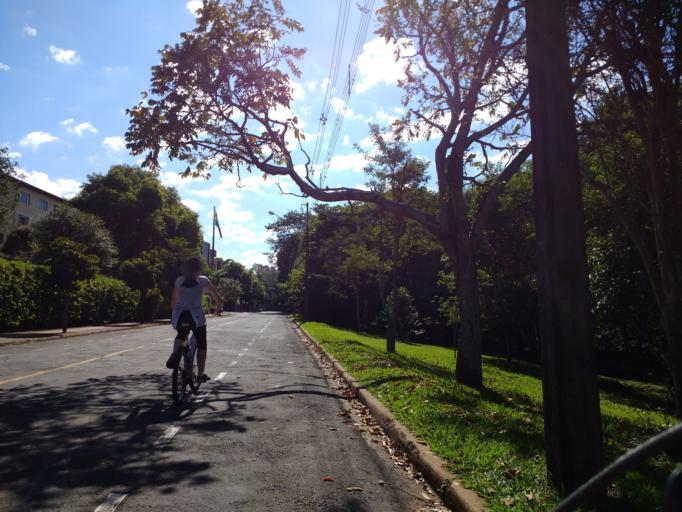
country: BR
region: Parana
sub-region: Londrina
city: Londrina
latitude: -23.3235
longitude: -51.1726
